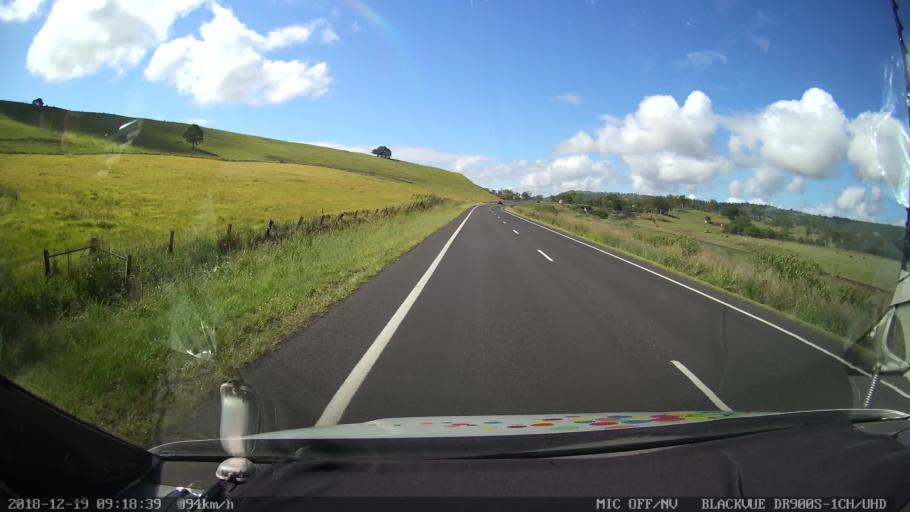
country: AU
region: New South Wales
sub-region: Kyogle
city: Kyogle
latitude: -28.5501
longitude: 152.9770
